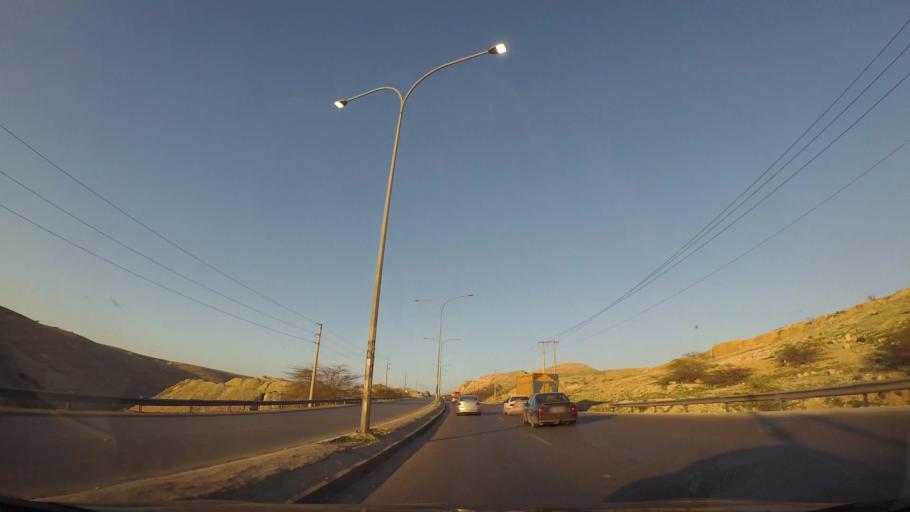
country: JO
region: Balqa
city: Yarqa
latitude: 31.8559
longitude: 35.7132
